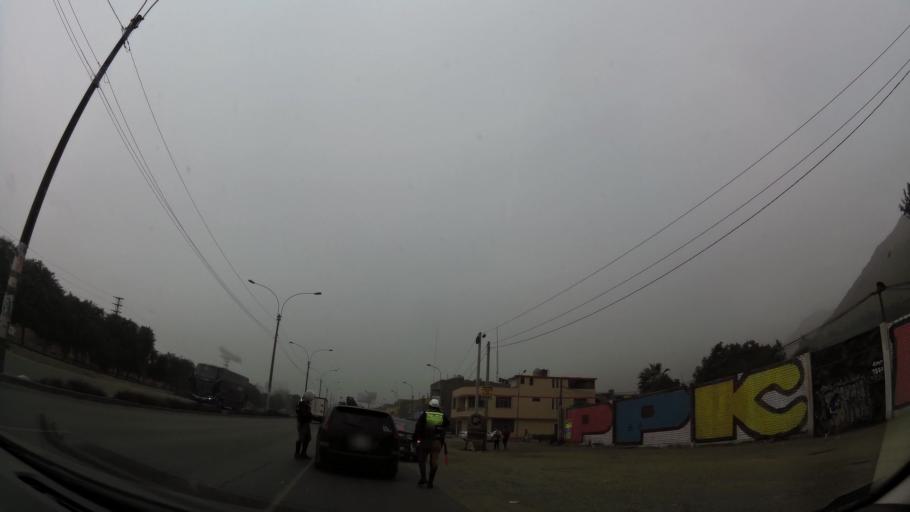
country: PE
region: Lima
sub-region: Lima
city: Chaclacayo
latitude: -11.9944
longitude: -76.8303
